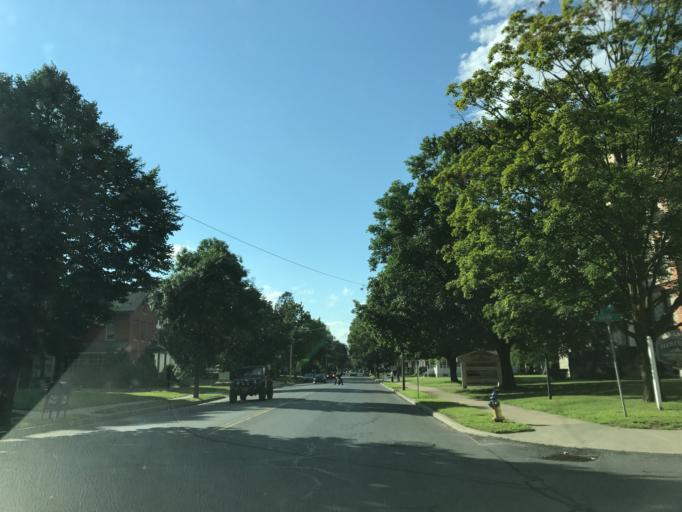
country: US
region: New York
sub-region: Warren County
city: Glens Falls
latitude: 43.3133
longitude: -73.6509
